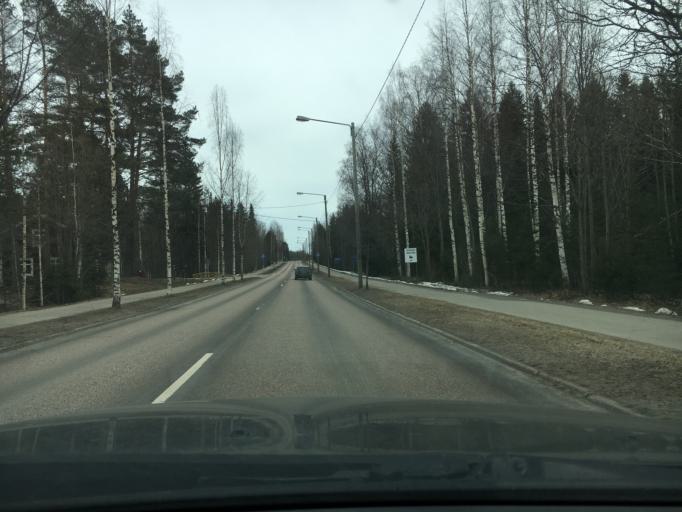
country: FI
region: Central Finland
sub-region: AEaenekoski
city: Konnevesi
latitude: 62.6278
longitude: 26.3111
